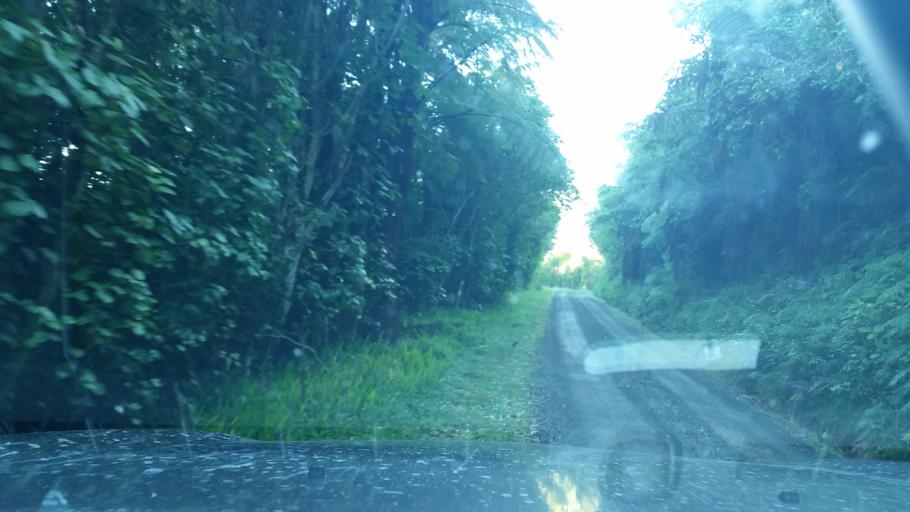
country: NZ
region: Marlborough
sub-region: Marlborough District
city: Picton
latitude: -41.1807
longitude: 173.9747
